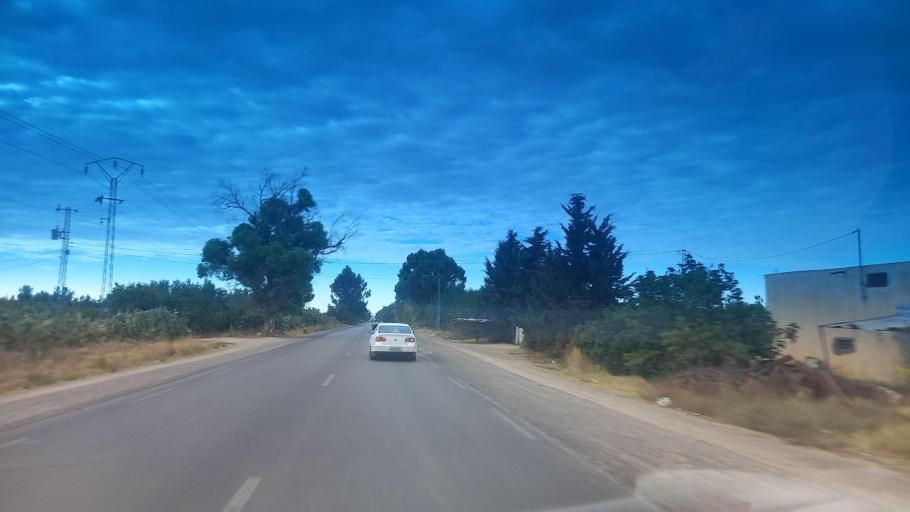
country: TN
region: Al Qasrayn
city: Sbiba
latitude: 35.2999
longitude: 9.0886
